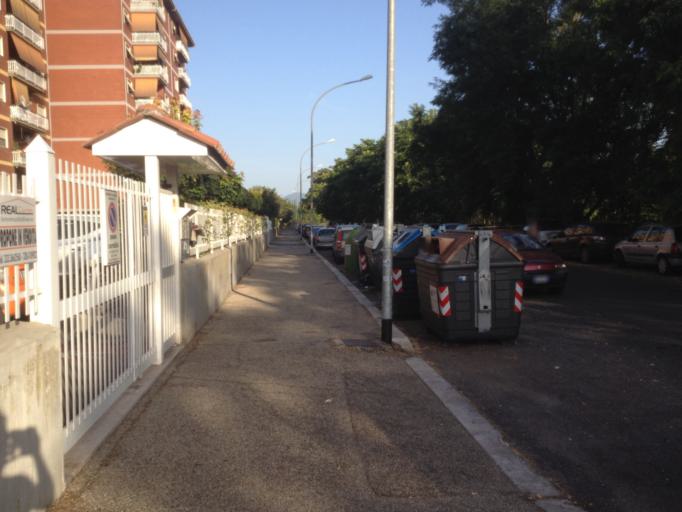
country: IT
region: Latium
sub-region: Citta metropolitana di Roma Capitale
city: Rome
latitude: 41.8658
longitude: 12.5759
